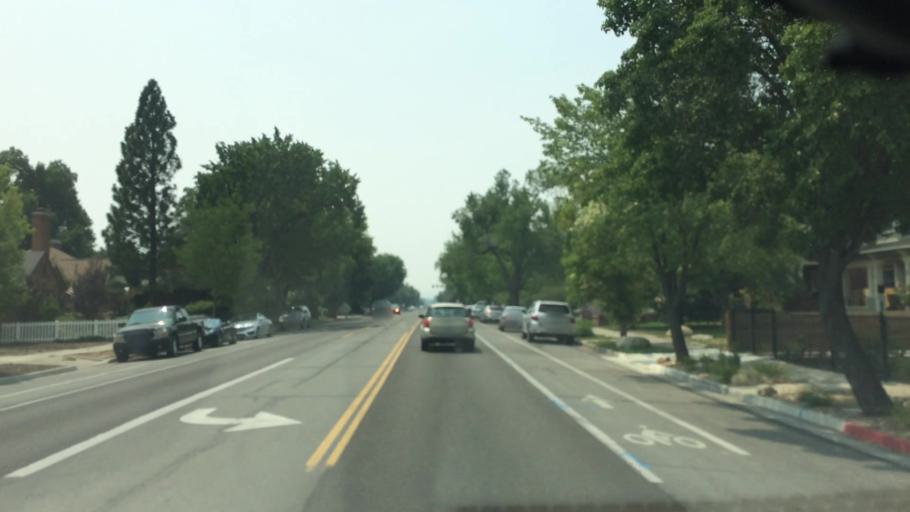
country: US
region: Nevada
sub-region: Washoe County
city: Reno
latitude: 39.5180
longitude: -119.8172
